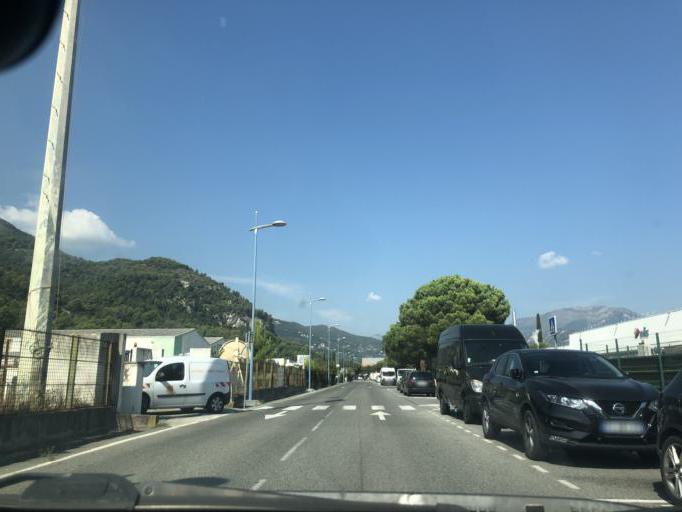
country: FR
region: Provence-Alpes-Cote d'Azur
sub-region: Departement des Alpes-Maritimes
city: Carros
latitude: 43.7933
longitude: 7.2025
